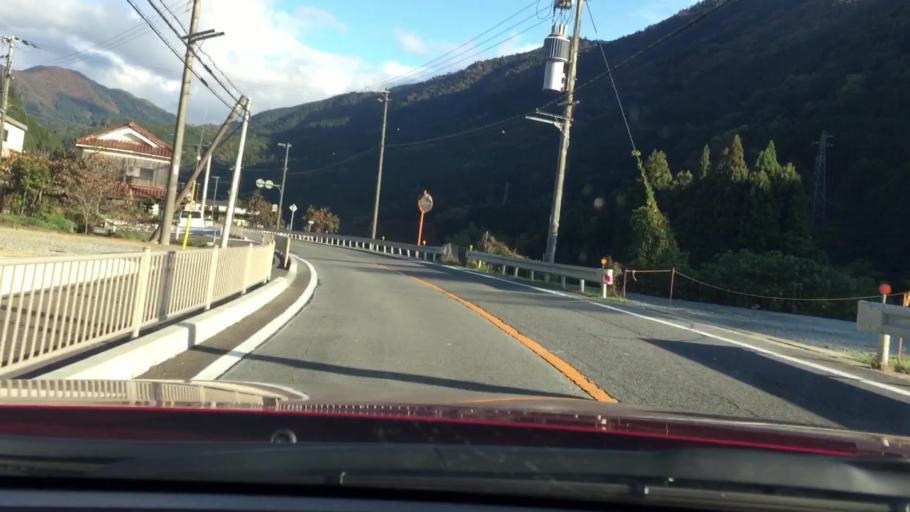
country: JP
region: Hyogo
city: Yamazakicho-nakabirose
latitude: 35.1206
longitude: 134.5691
